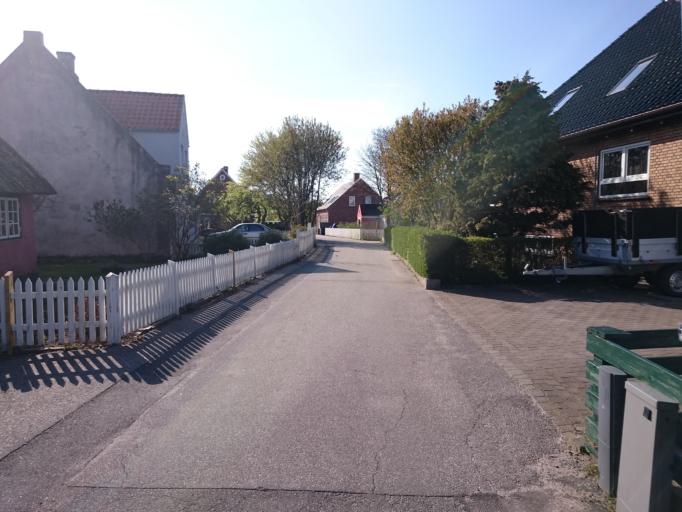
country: DK
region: South Denmark
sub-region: Fano Kommune
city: Nordby
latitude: 55.4501
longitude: 8.4050
